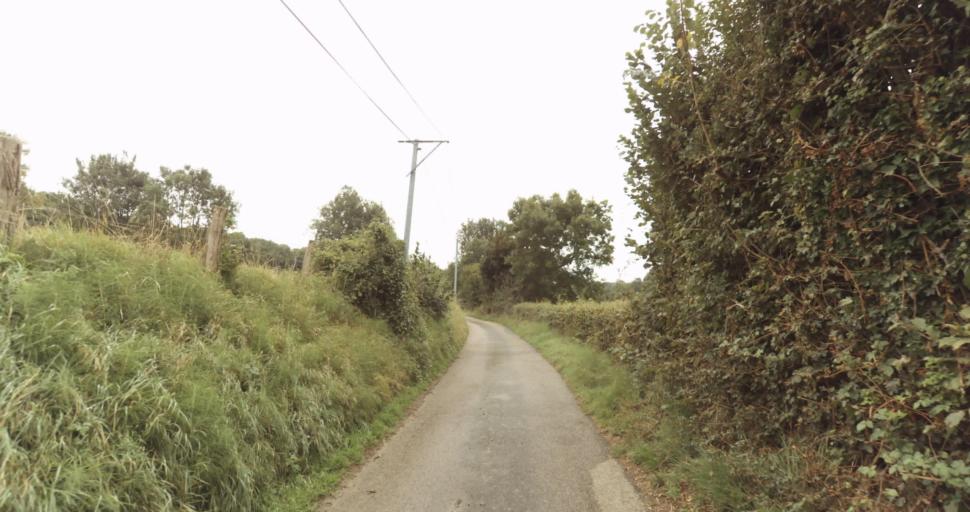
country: FR
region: Lower Normandy
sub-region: Departement de l'Orne
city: Vimoutiers
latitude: 48.8724
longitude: 0.2133
